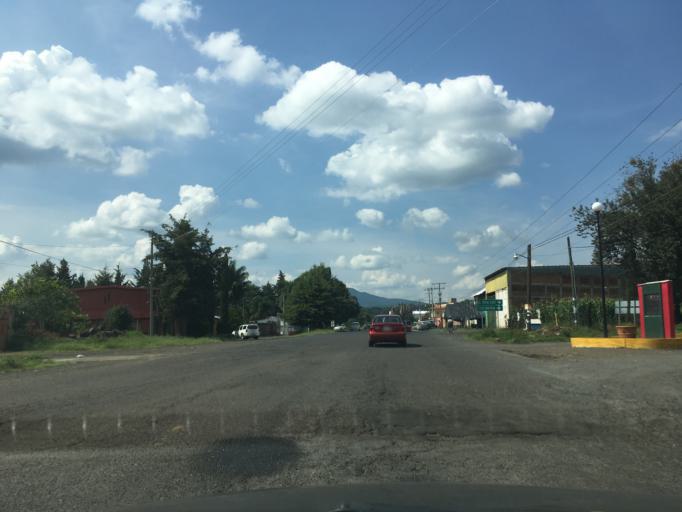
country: MX
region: Michoacan
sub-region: Tingueindin
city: Tingueindin
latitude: 19.7728
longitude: -102.4994
